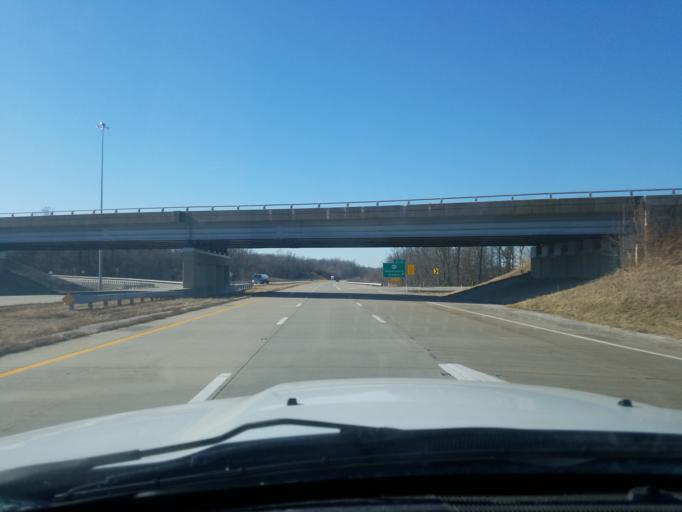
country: US
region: Indiana
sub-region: Warrick County
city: Newburgh
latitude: 37.7524
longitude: -87.3954
